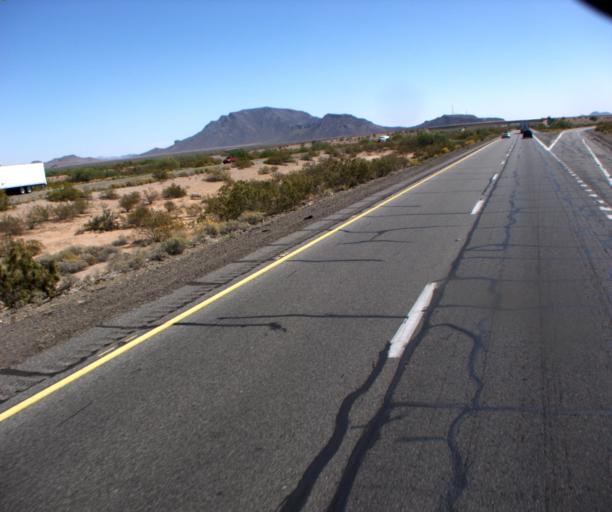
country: US
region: Arizona
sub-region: La Paz County
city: Salome
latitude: 33.5389
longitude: -113.1620
